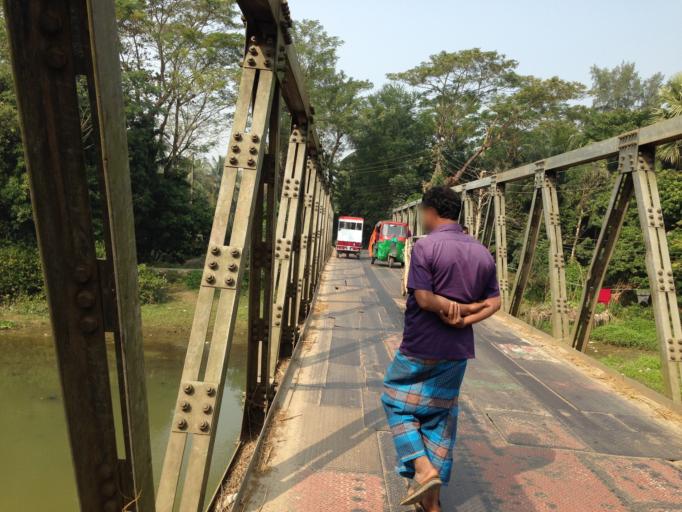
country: BD
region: Chittagong
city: Lakshmipur
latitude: 22.9325
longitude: 90.8140
